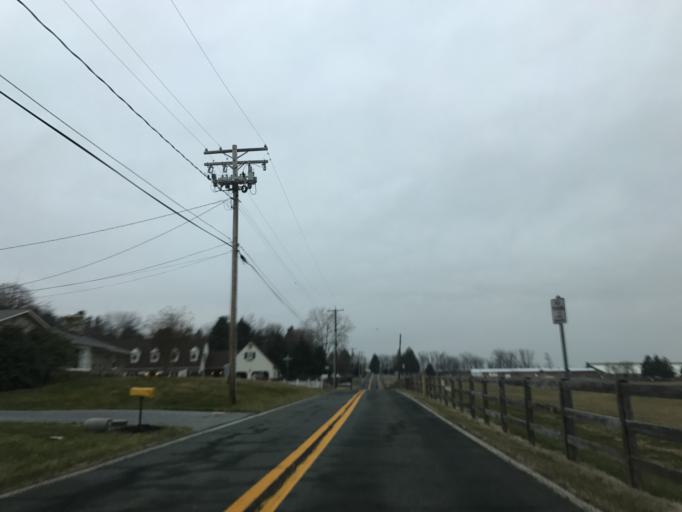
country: US
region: Maryland
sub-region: Carroll County
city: Westminster
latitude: 39.5539
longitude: -76.9958
